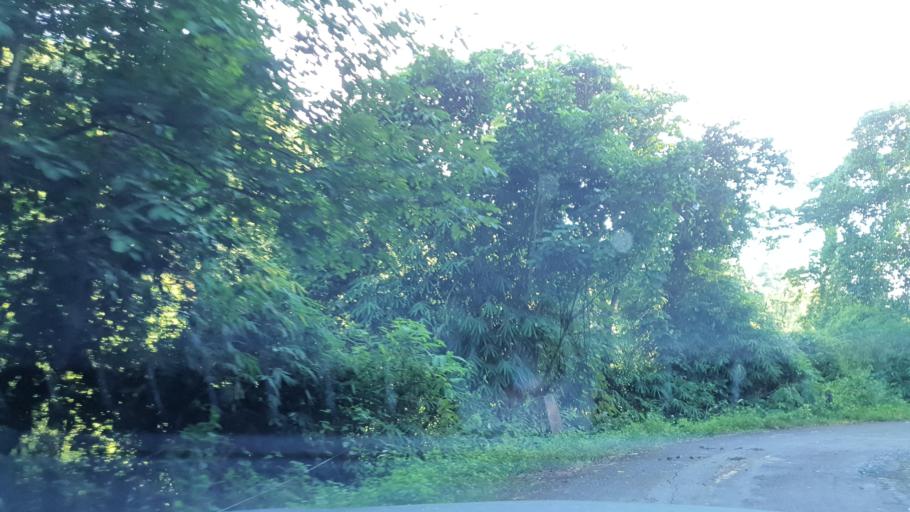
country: TH
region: Chiang Mai
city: Mae On
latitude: 18.8146
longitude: 99.3350
